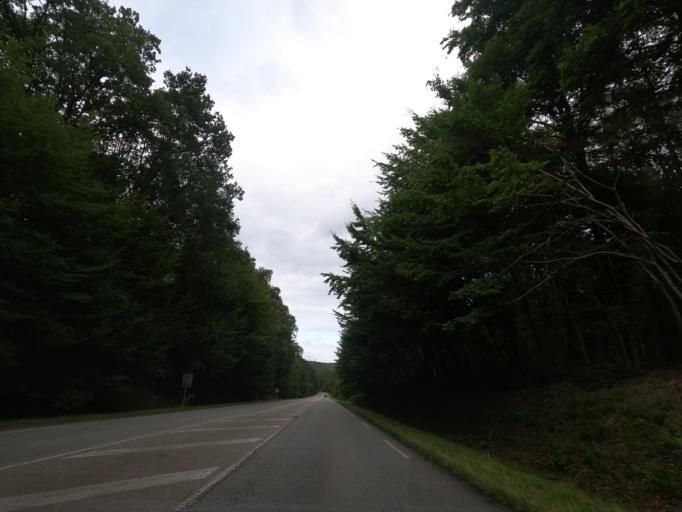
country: FR
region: Haute-Normandie
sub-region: Departement de l'Eure
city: Saint-Ouen-de-Thouberville
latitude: 49.3279
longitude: 0.9112
